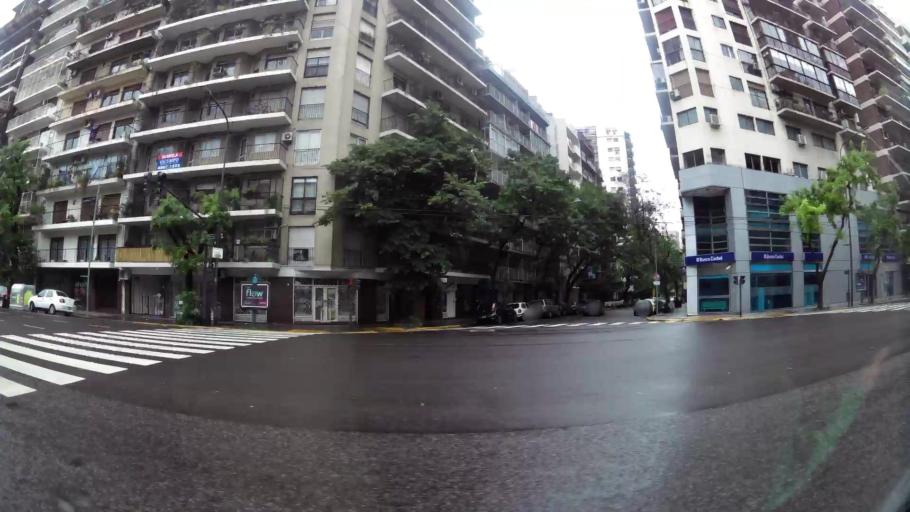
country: AR
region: Buenos Aires F.D.
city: Retiro
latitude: -34.5835
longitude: -58.4054
